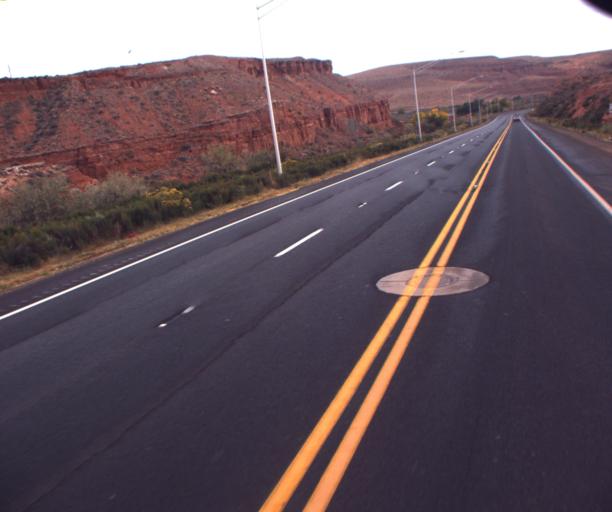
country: US
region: Arizona
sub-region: Coconino County
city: Tuba City
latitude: 36.1149
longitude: -111.2326
